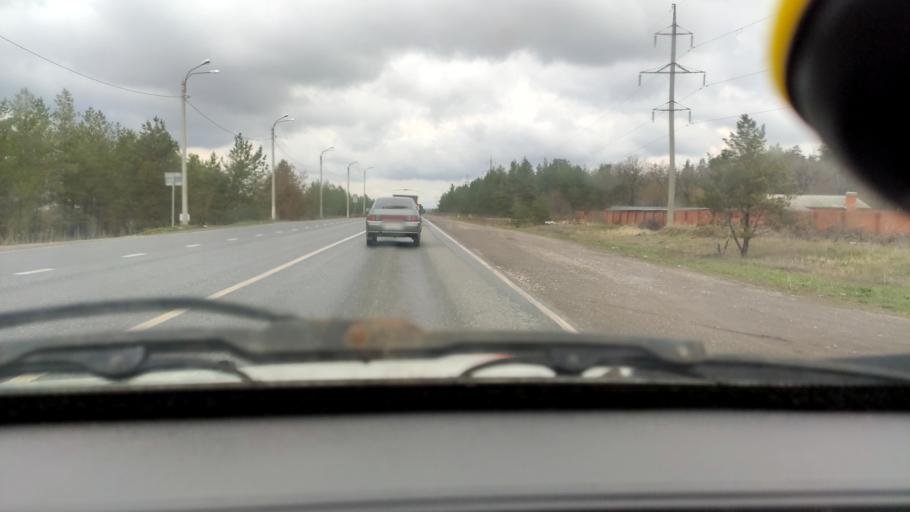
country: RU
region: Samara
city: Zhigulevsk
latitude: 53.5674
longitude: 49.5483
